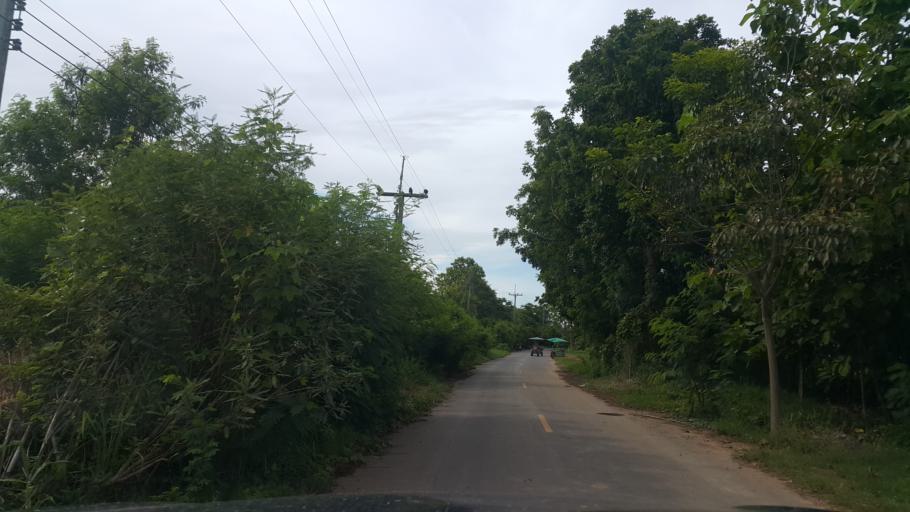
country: TH
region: Sukhothai
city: Si Nakhon
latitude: 17.2684
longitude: 99.9264
